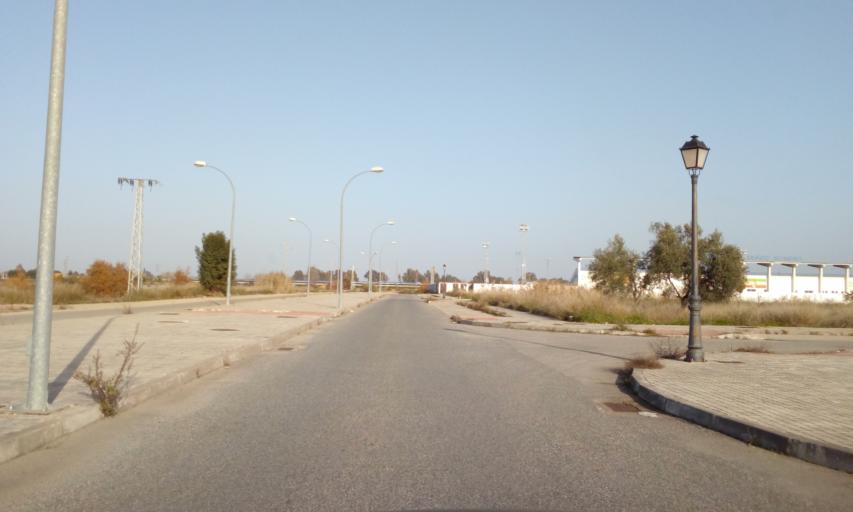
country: ES
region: Andalusia
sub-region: Provincia de Sevilla
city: Santiponce
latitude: 37.4451
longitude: -6.0443
